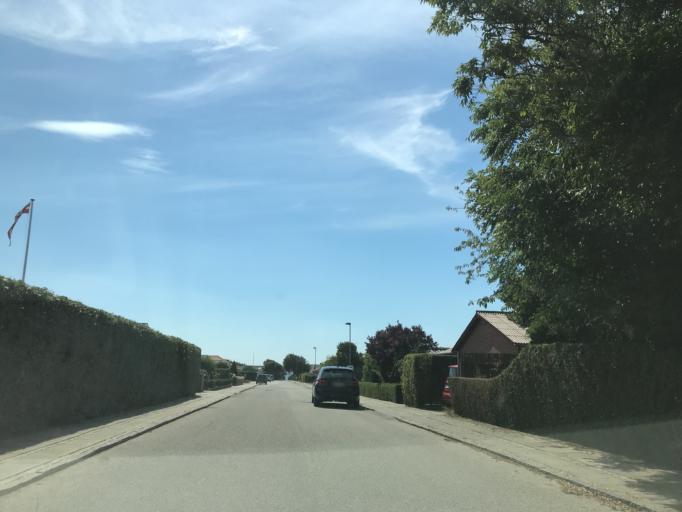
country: DK
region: Central Jutland
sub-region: Ringkobing-Skjern Kommune
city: Ringkobing
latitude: 56.0839
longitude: 8.2550
